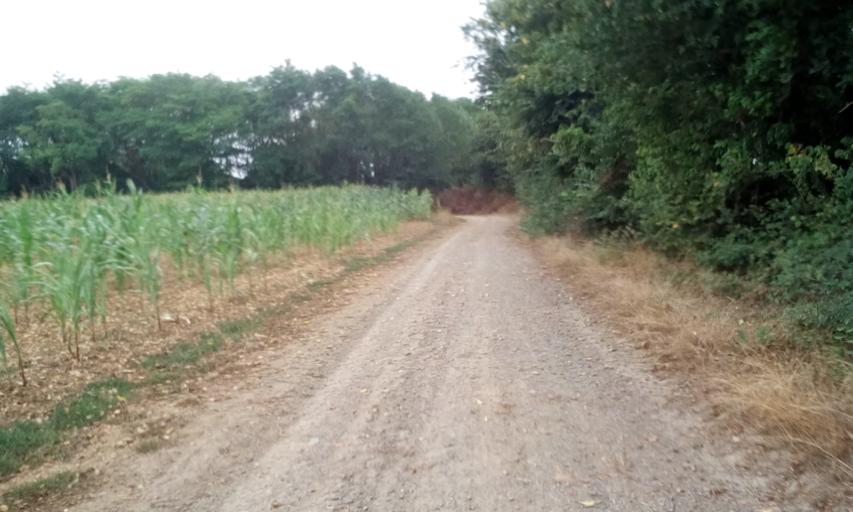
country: FR
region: Lower Normandy
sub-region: Departement du Calvados
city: Eterville
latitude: 49.1411
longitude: -0.4401
